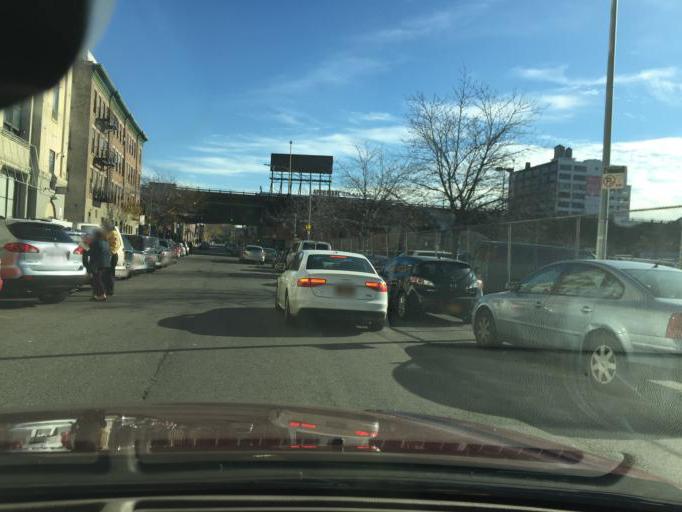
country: US
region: New York
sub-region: Kings County
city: Bensonhurst
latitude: 40.6556
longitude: -74.0081
